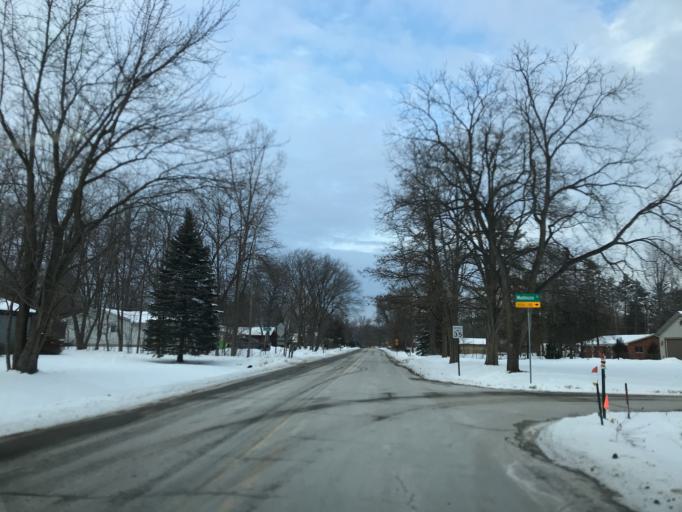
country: US
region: Michigan
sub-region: Livingston County
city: Whitmore Lake
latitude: 42.3946
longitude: -83.7529
